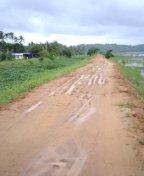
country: IN
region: Kerala
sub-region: Thrissur District
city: Trichur
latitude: 10.4787
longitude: 76.2131
